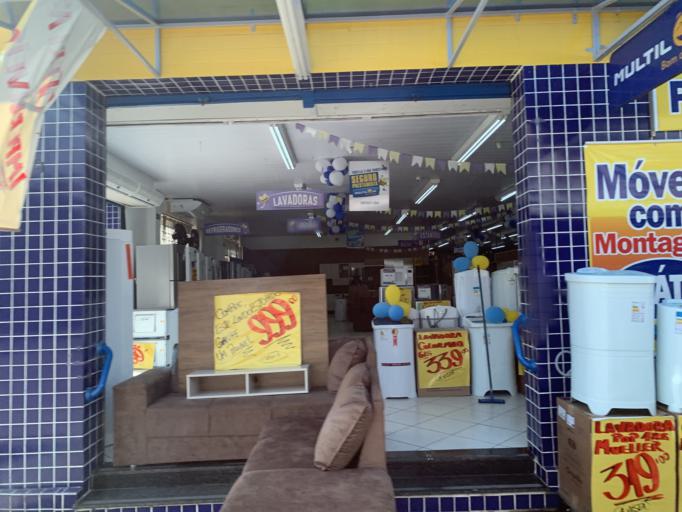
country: BR
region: Parana
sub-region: Antonina
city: Antonina
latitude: -25.4306
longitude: -48.7140
